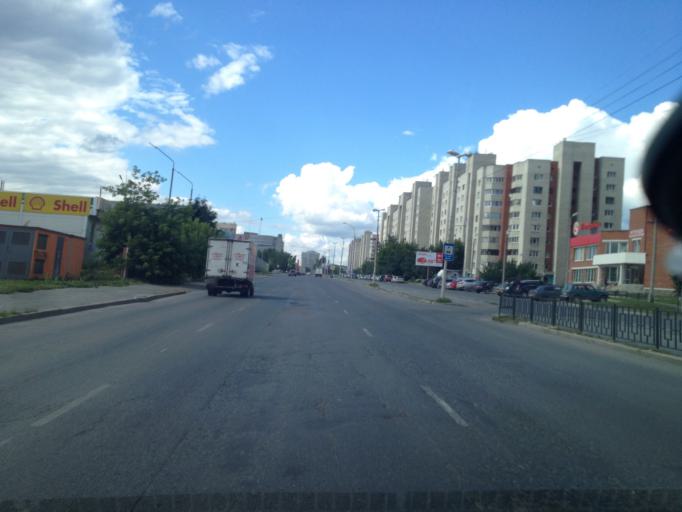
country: RU
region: Sverdlovsk
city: Yekaterinburg
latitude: 56.8486
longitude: 60.5591
